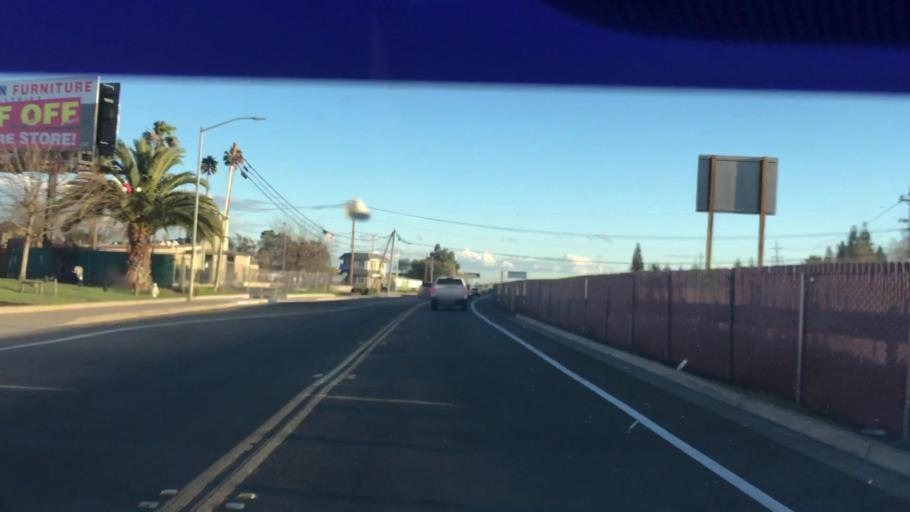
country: US
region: California
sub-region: Sacramento County
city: Florin
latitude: 38.4661
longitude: -121.4141
